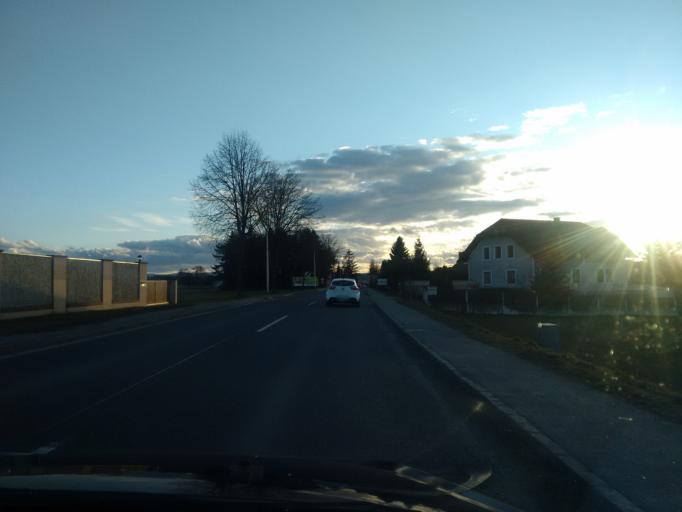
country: AT
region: Lower Austria
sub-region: Politischer Bezirk Melk
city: Erlauf
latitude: 48.1883
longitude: 15.1900
